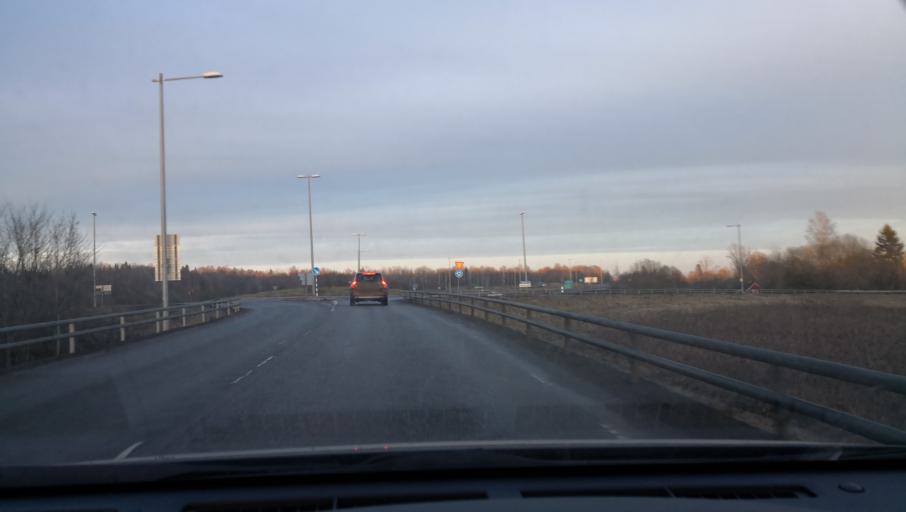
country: SE
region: OErebro
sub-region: Orebro Kommun
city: Vintrosa
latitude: 59.2434
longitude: 14.9417
